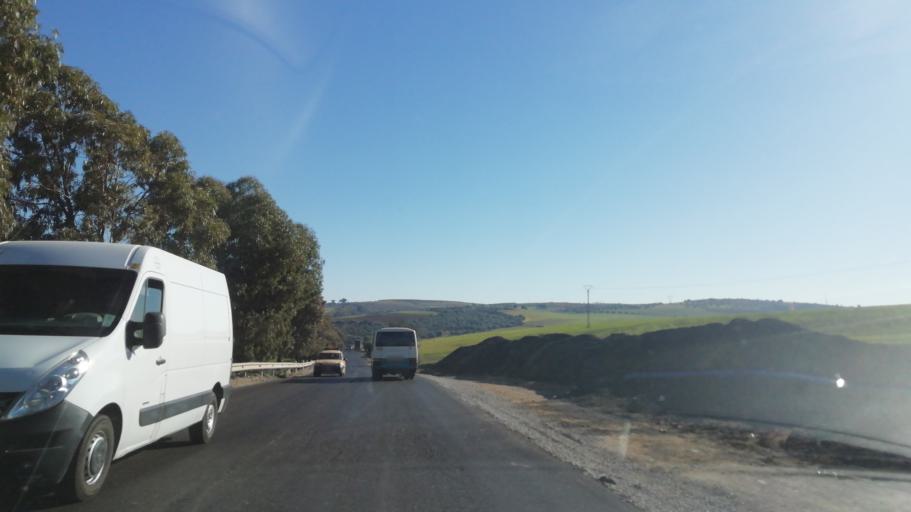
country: DZ
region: Relizane
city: Smala
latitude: 35.6727
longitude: 0.8042
